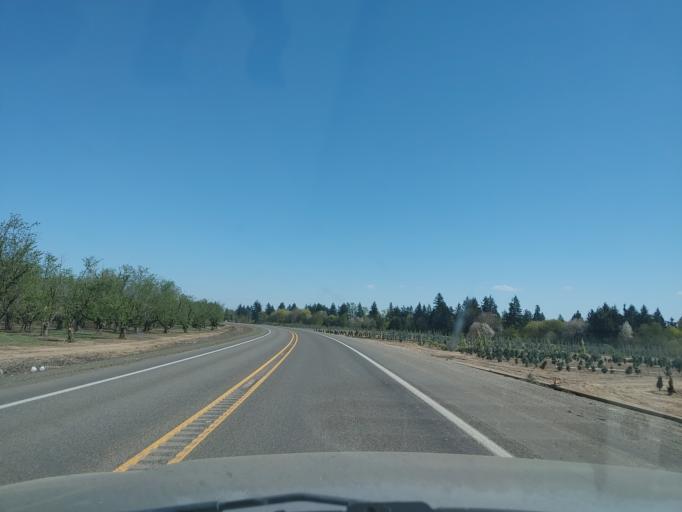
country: US
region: Oregon
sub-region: Yamhill County
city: Newberg
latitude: 45.2433
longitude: -122.9384
